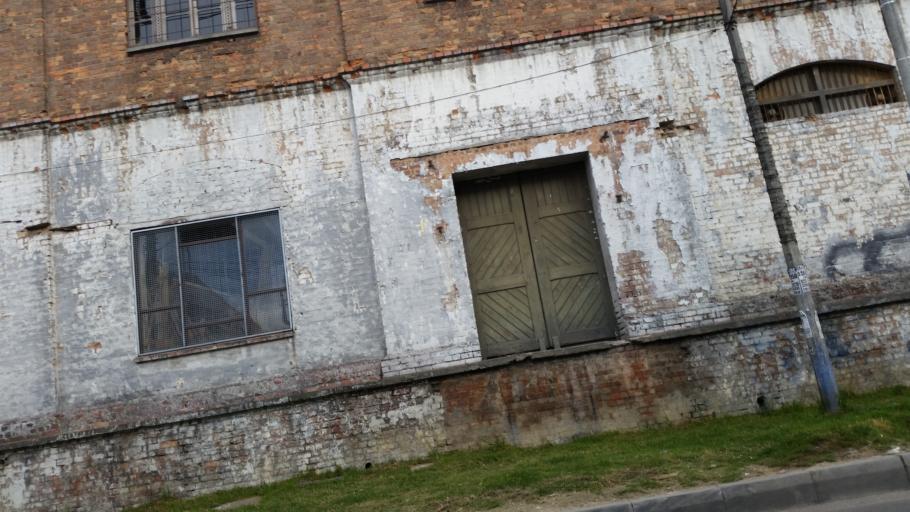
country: CO
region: Bogota D.C.
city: Bogota
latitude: 4.6083
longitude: -74.0840
